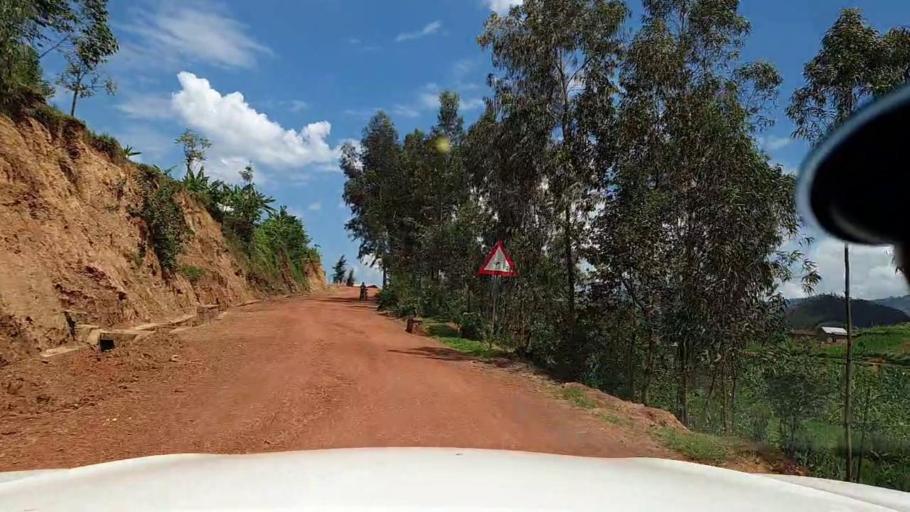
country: RW
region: Northern Province
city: Byumba
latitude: -1.7382
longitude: 29.8623
